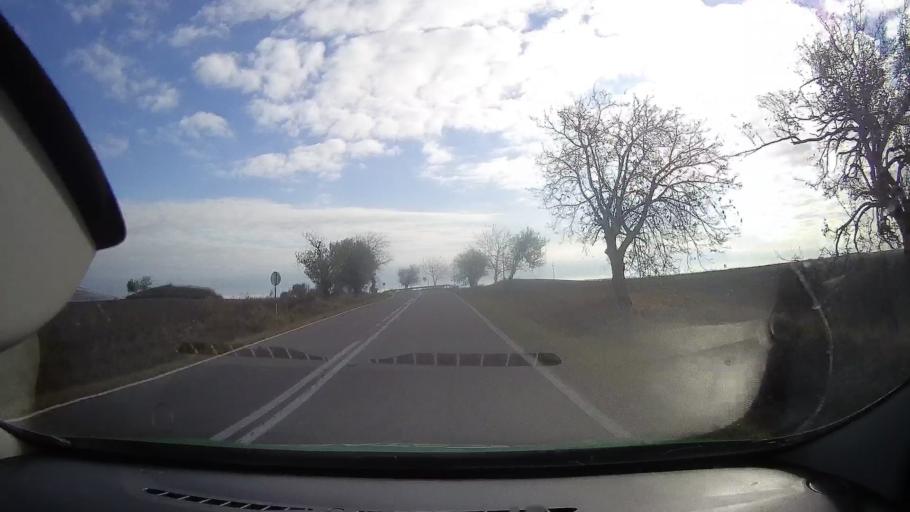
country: RO
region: Tulcea
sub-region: Comuna Bestepe
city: Bestepe
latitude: 45.0783
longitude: 29.0426
